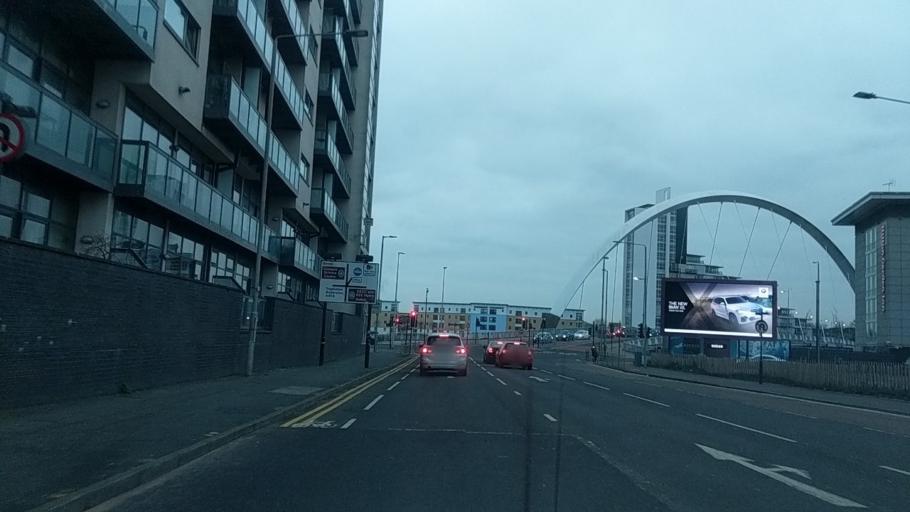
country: GB
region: Scotland
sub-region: Glasgow City
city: Glasgow
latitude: 55.8586
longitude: -4.2814
